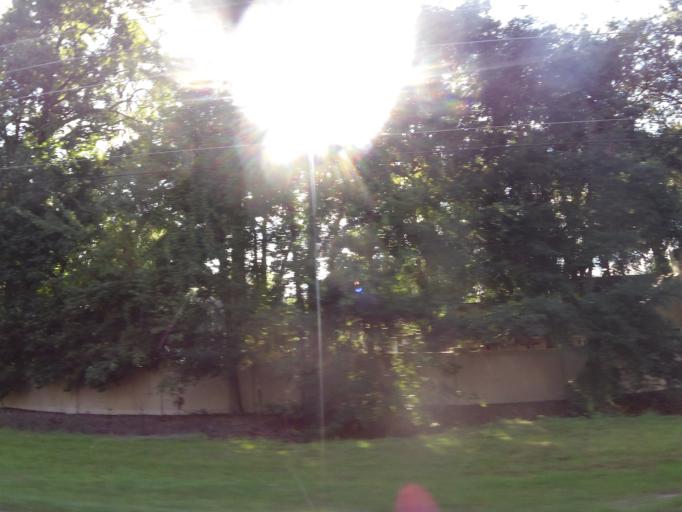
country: US
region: Georgia
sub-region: Glynn County
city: Saint Simon Mills
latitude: 31.2005
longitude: -81.3761
